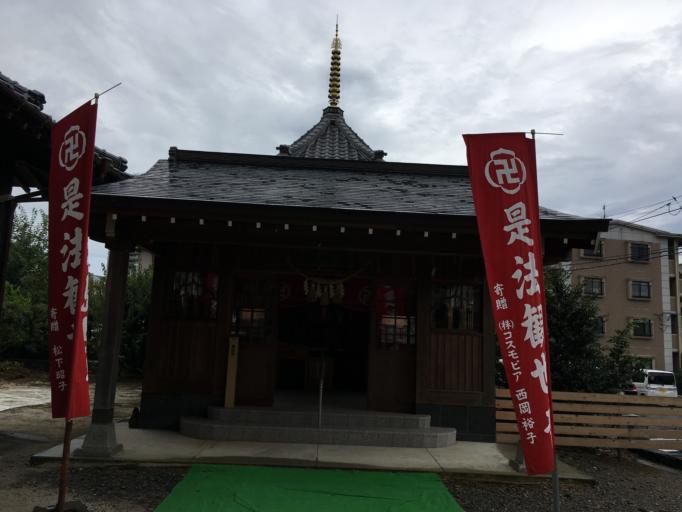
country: JP
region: Kumamoto
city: Kumamoto
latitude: 32.8002
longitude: 130.7239
